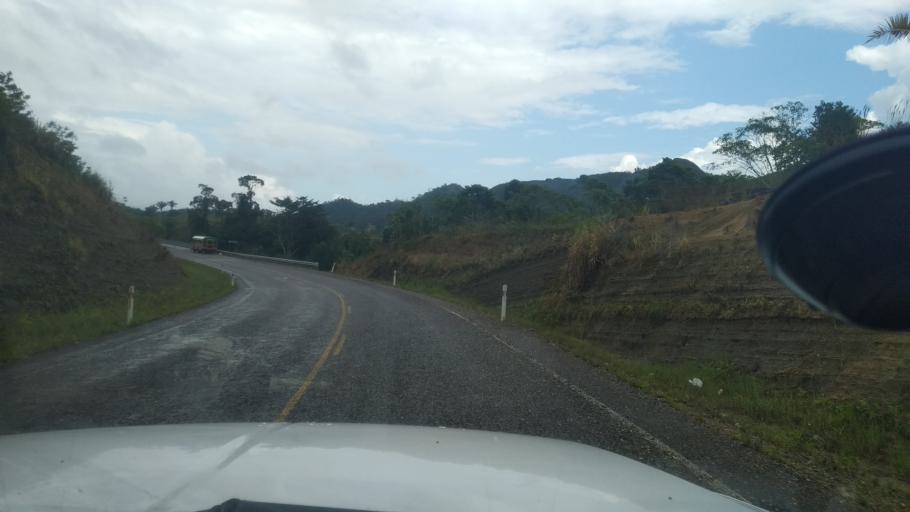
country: GT
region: Peten
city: San Luis
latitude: 16.1834
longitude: -89.2005
